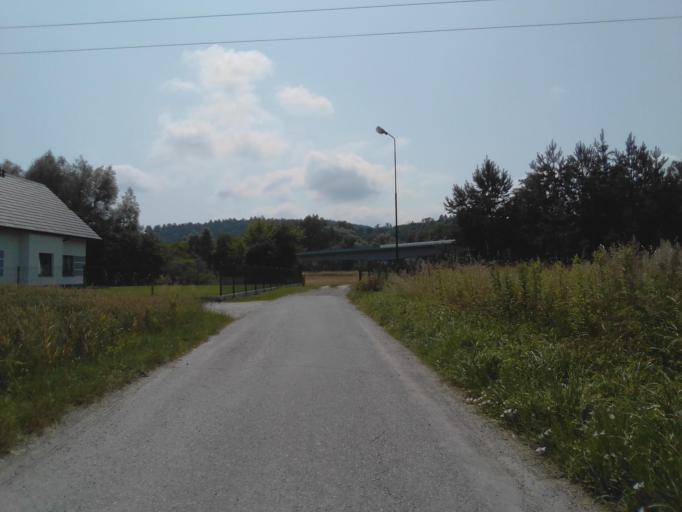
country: PL
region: Subcarpathian Voivodeship
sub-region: Powiat strzyzowski
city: Czudec
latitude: 49.9416
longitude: 21.8236
